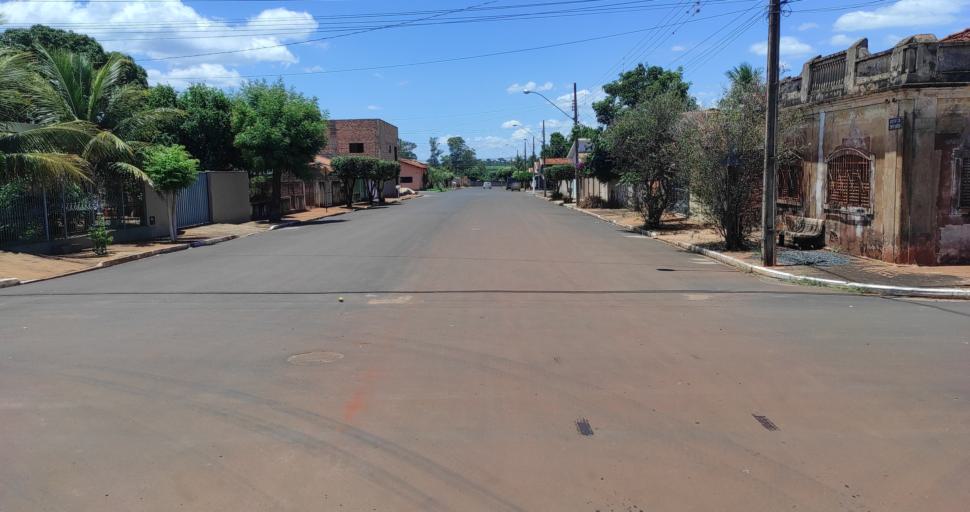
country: BR
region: Minas Gerais
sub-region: Frutal
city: Frutal
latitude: -20.1418
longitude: -48.7020
